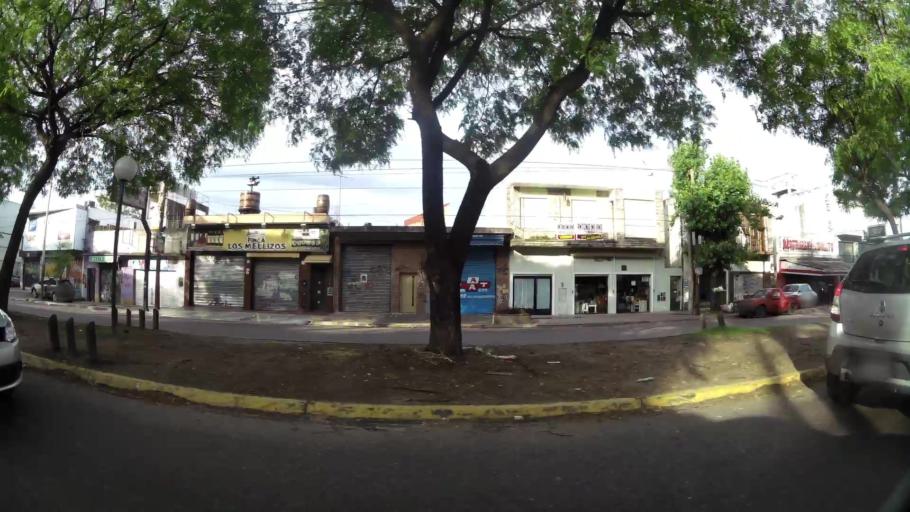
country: AR
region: Buenos Aires
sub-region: Partido de Moron
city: Moron
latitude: -34.6420
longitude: -58.6233
